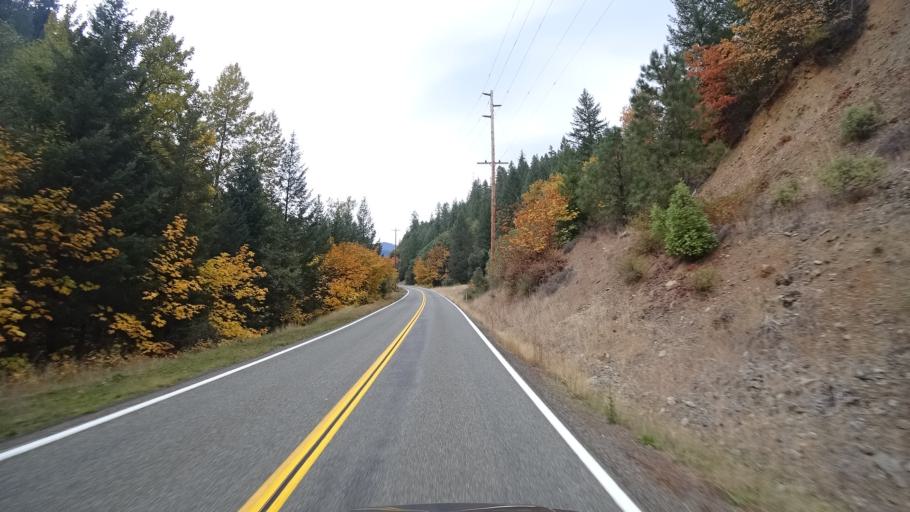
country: US
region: California
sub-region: Siskiyou County
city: Happy Camp
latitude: 41.9081
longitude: -123.4438
